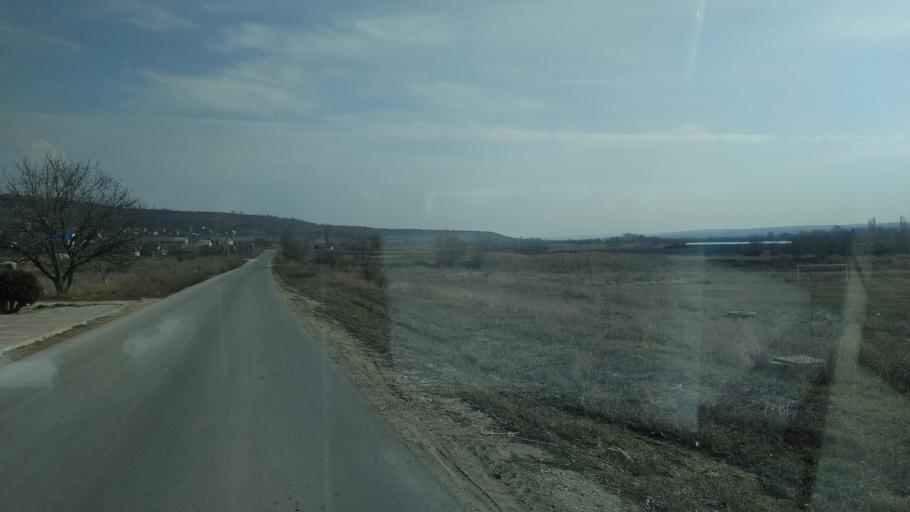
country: MD
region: Chisinau
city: Singera
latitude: 46.9251
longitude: 29.0680
